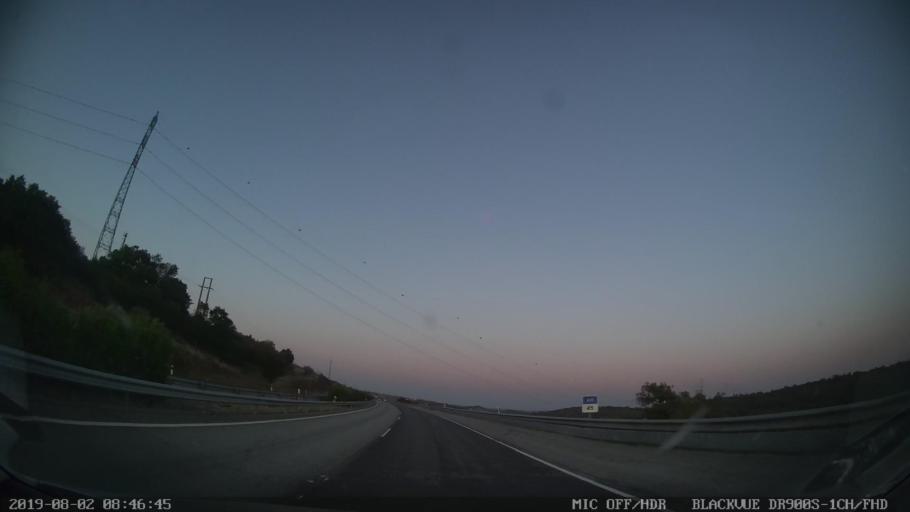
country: PT
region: Santarem
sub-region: Abrantes
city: Alferrarede
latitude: 39.4848
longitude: -8.1428
